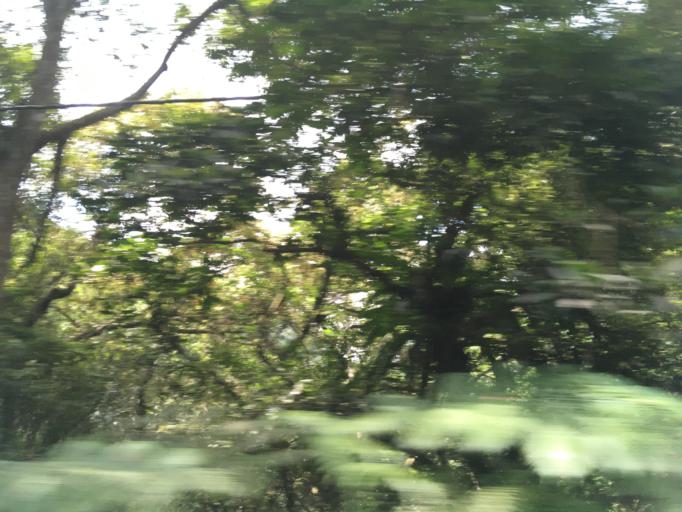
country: TW
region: Taipei
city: Taipei
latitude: 24.9392
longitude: 121.5765
